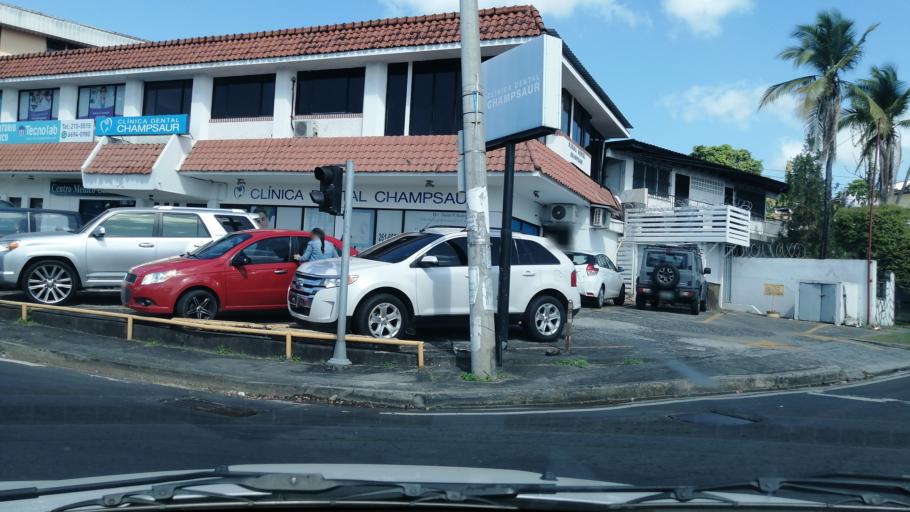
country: PA
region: Panama
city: Panama
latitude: 9.0118
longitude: -79.5256
